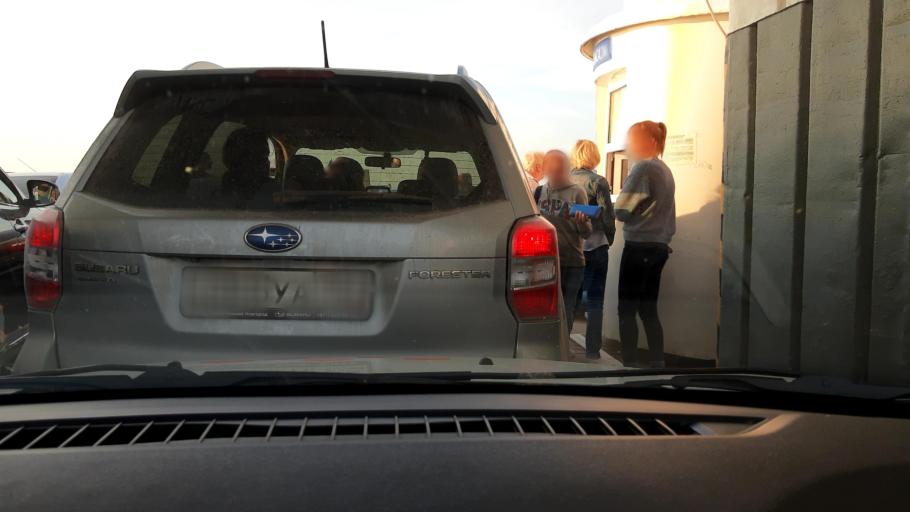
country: RU
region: Nizjnij Novgorod
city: Nizhniy Novgorod
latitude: 56.3323
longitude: 44.0232
